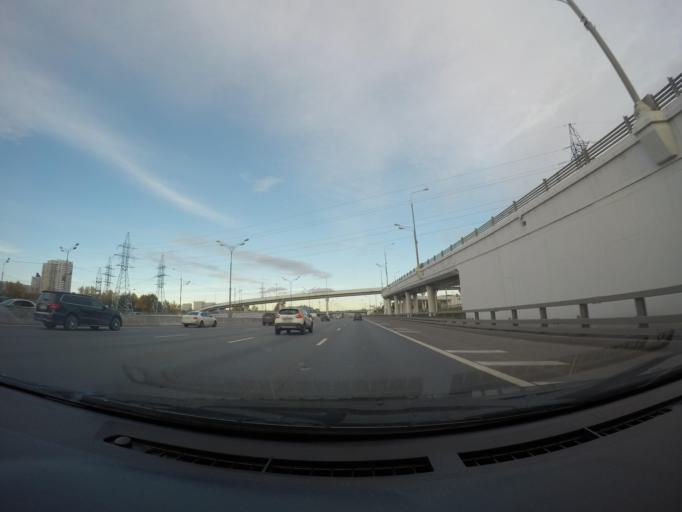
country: RU
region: Moskovskaya
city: Razvilka
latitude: 55.5895
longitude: 37.7246
